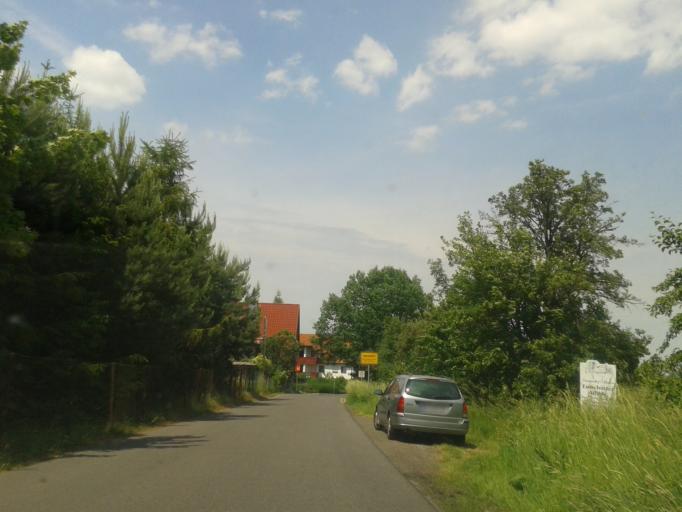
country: DE
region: Saxony
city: Bannewitz
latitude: 50.9928
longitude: 13.7292
